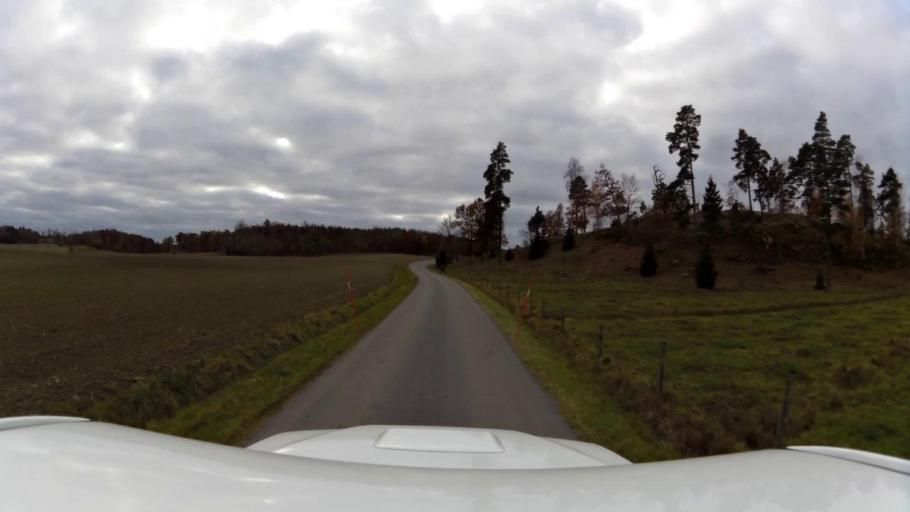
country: SE
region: OEstergoetland
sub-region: Linkopings Kommun
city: Linghem
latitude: 58.3864
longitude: 15.8360
